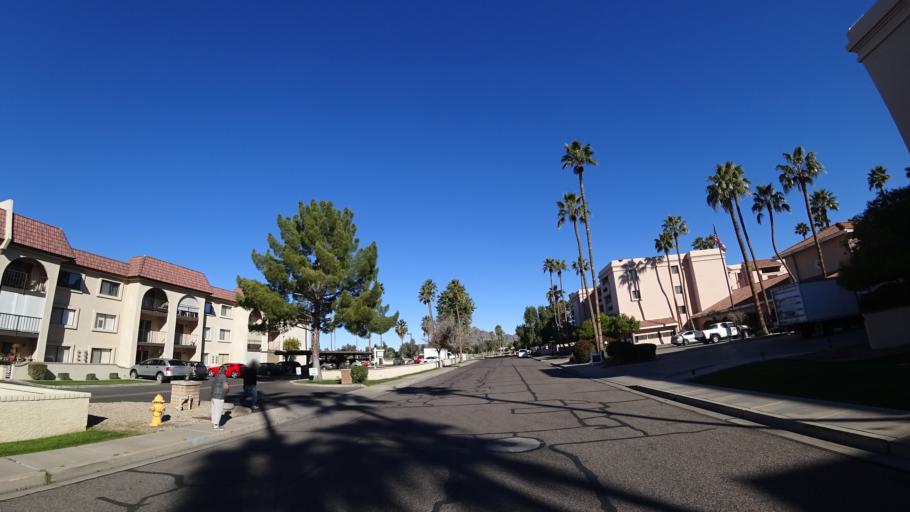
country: US
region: Arizona
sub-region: Maricopa County
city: Phoenix
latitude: 33.4960
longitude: -112.0163
